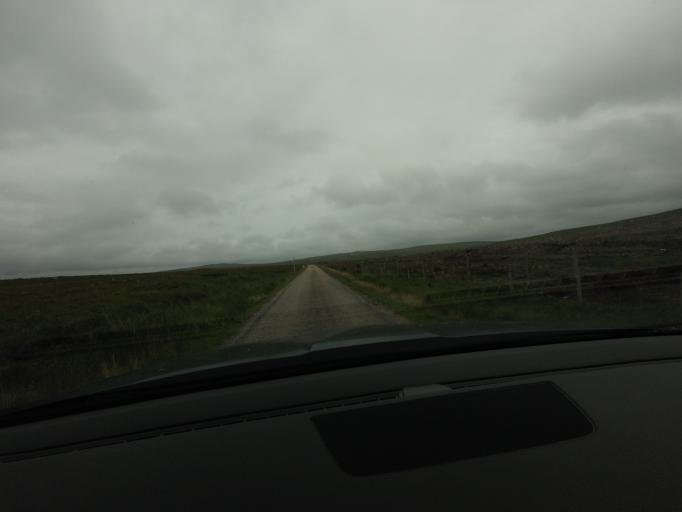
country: GB
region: Scotland
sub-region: Highland
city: Golspie
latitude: 58.2999
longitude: -4.4363
